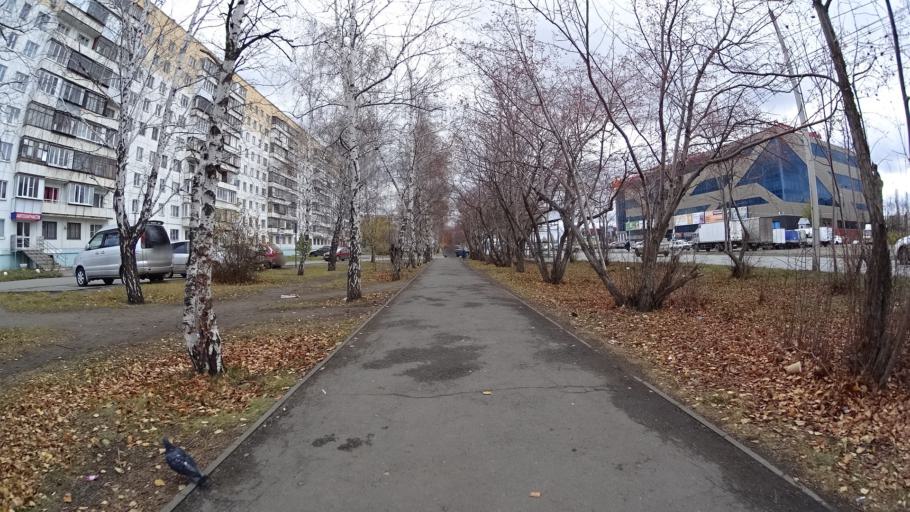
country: RU
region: Chelyabinsk
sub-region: Gorod Chelyabinsk
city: Chelyabinsk
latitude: 55.1912
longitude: 61.3217
